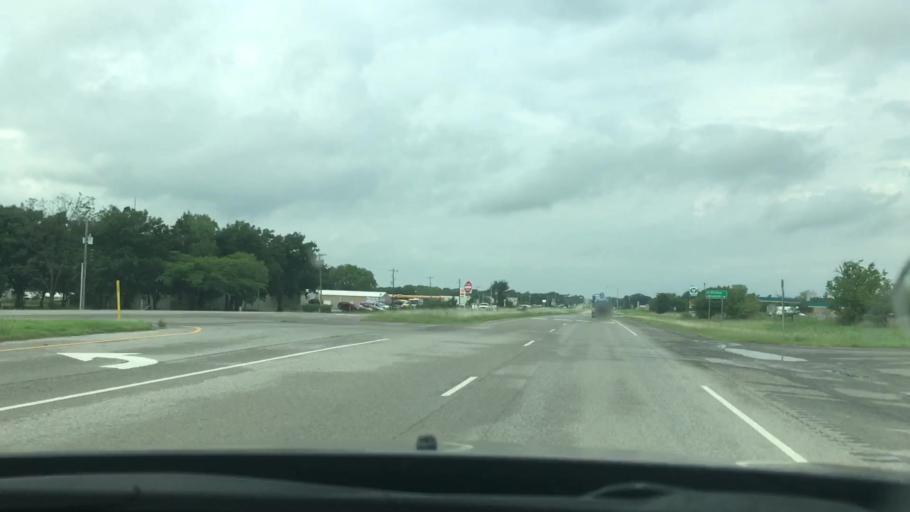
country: US
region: Oklahoma
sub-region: Carter County
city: Wilson
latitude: 34.1731
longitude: -97.4715
